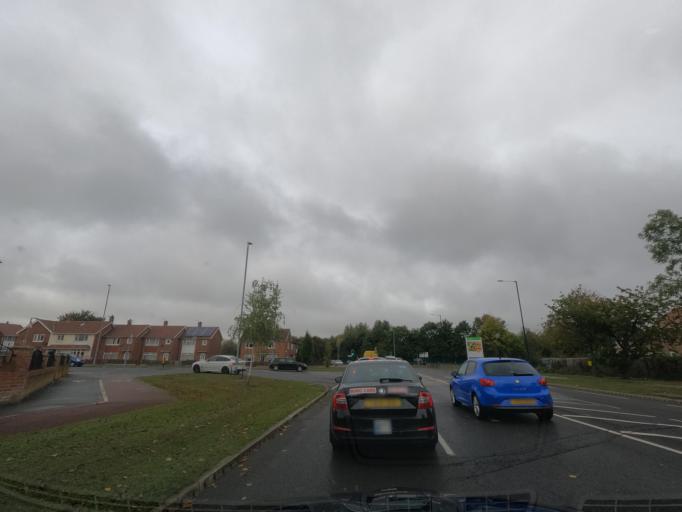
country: GB
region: England
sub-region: Middlesbrough
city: Nunthorpe
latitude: 54.5636
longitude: -1.1913
